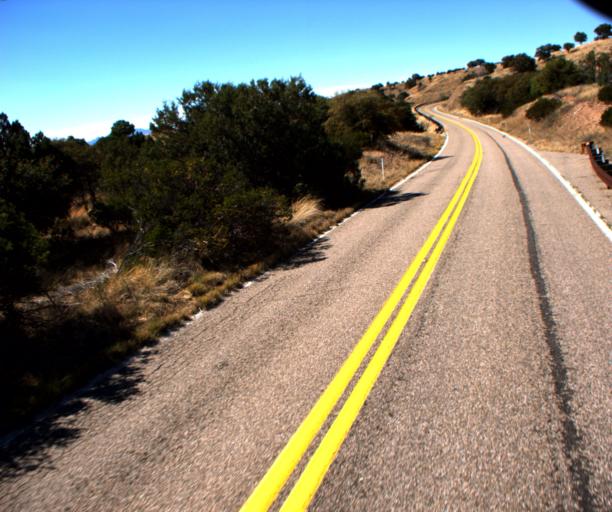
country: US
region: Arizona
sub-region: Cochise County
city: Sierra Vista
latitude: 31.4960
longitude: -110.4931
